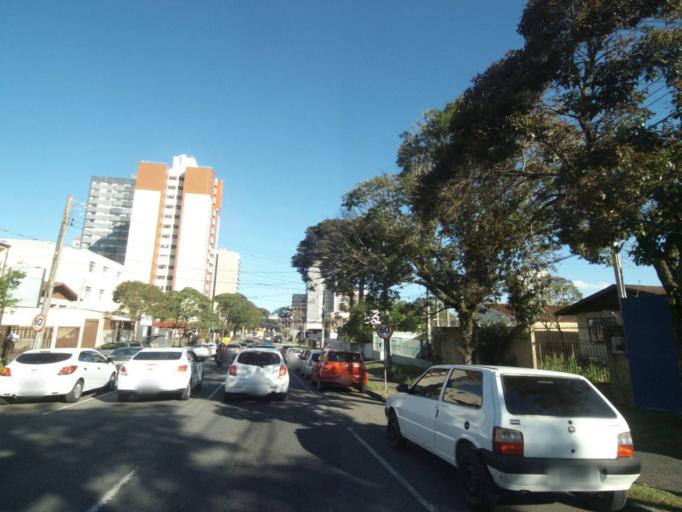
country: BR
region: Parana
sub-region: Curitiba
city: Curitiba
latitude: -25.3994
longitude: -49.2482
